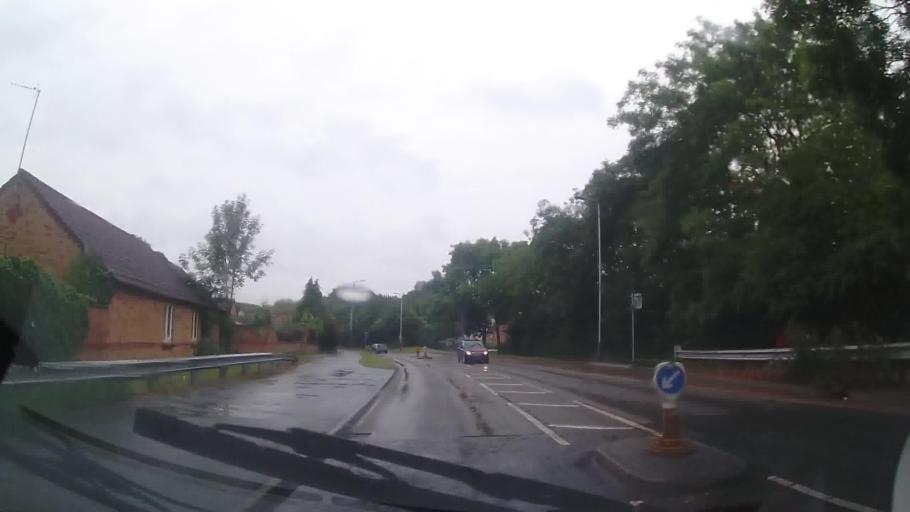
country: GB
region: England
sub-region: Leicestershire
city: Anstey
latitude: 52.6696
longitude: -1.1706
